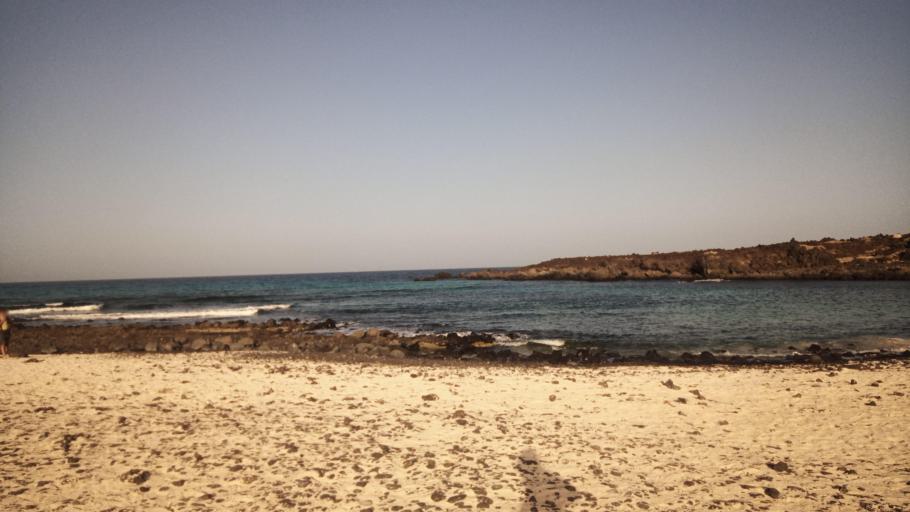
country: ES
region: Canary Islands
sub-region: Provincia de Las Palmas
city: Haria
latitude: 29.2081
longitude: -13.4296
